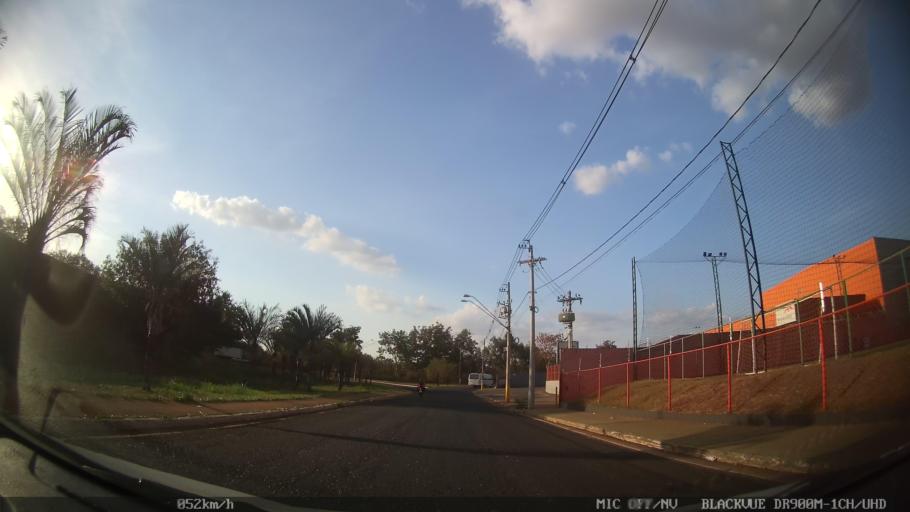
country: BR
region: Sao Paulo
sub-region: Ribeirao Preto
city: Ribeirao Preto
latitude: -21.1385
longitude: -47.8028
